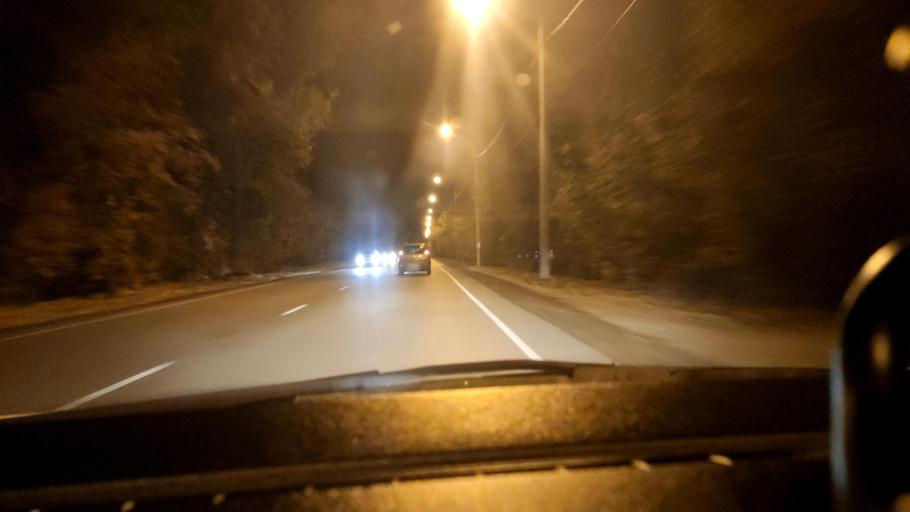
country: RU
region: Voronezj
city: Voronezh
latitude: 51.5992
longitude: 39.1770
